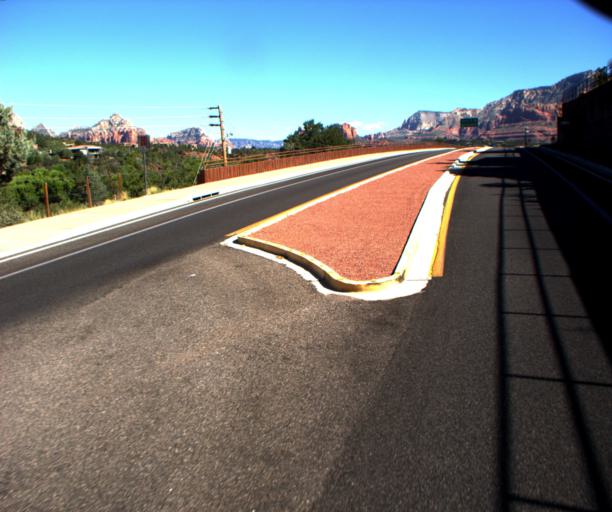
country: US
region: Arizona
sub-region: Coconino County
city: Sedona
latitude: 34.8535
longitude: -111.7642
